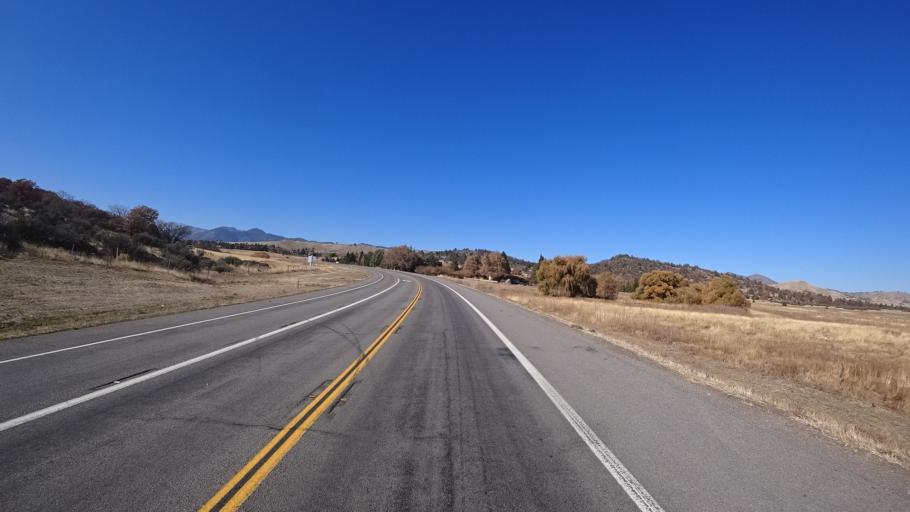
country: US
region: California
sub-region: Siskiyou County
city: Yreka
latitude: 41.7414
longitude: -122.5993
